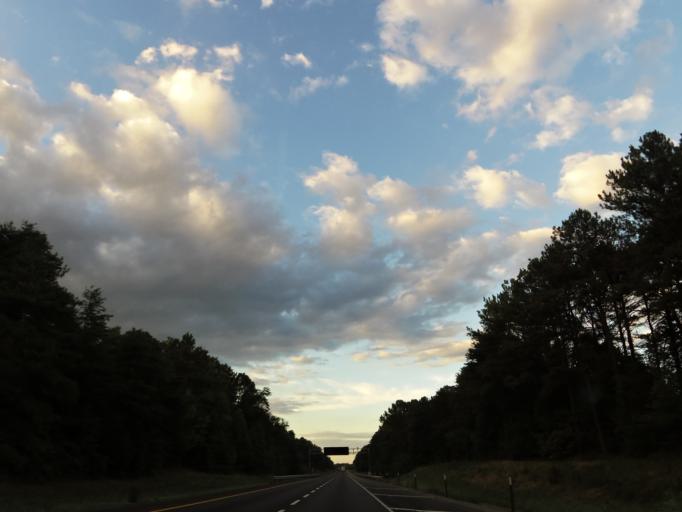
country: US
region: Tennessee
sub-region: Bradley County
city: Hopewell
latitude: 35.2671
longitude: -84.8273
